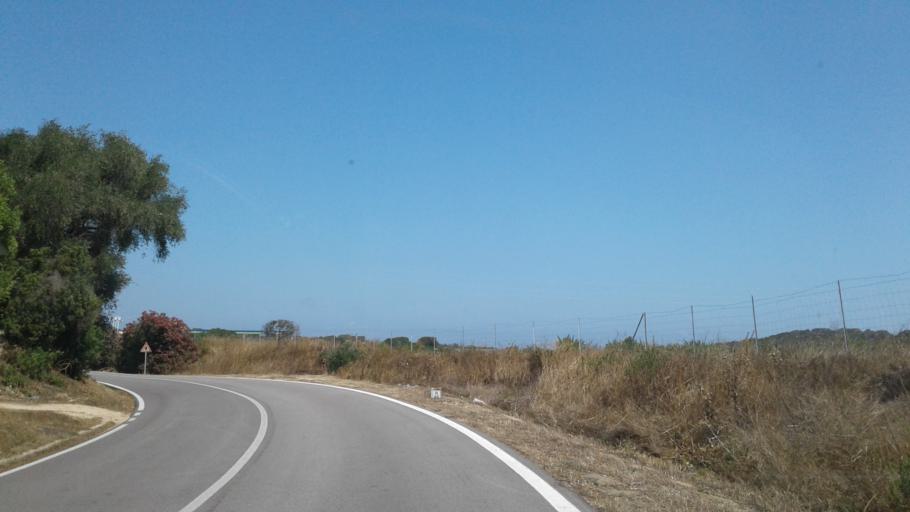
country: IT
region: Sardinia
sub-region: Provincia di Olbia-Tempio
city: Palau
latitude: 41.1603
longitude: 9.3140
